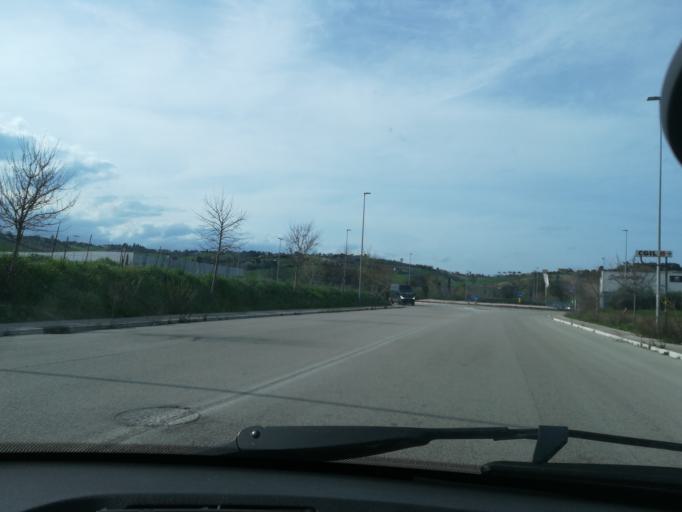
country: IT
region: The Marches
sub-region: Provincia di Macerata
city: Piediripa
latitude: 43.2821
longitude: 13.4972
